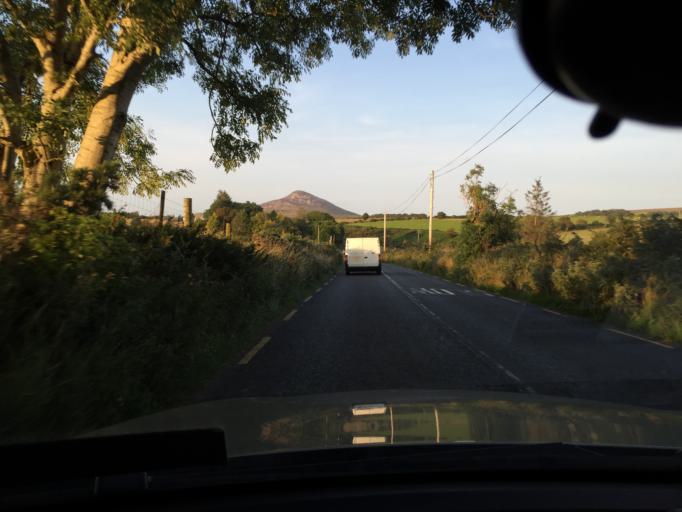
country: IE
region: Leinster
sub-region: Wicklow
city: Kilmacanoge
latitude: 53.1291
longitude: -6.1794
